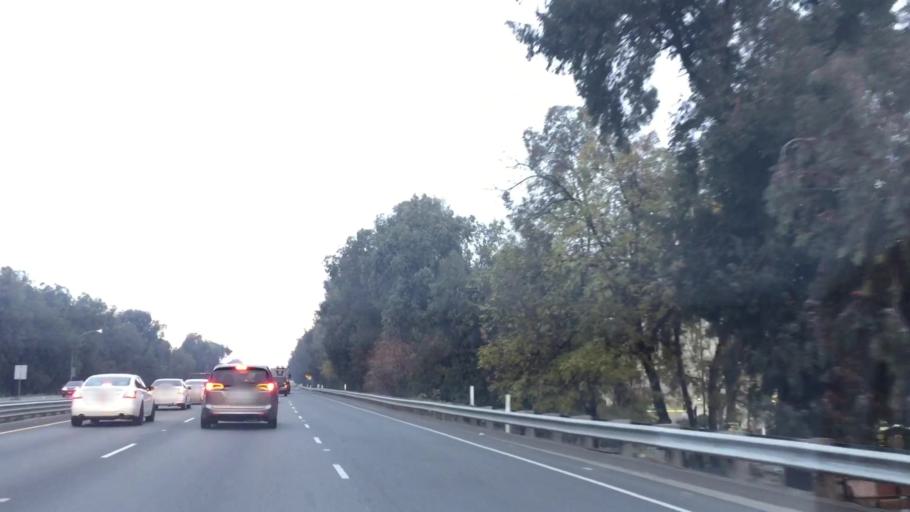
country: US
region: California
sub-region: Yuba County
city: Marysville
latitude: 39.1249
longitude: -121.5777
